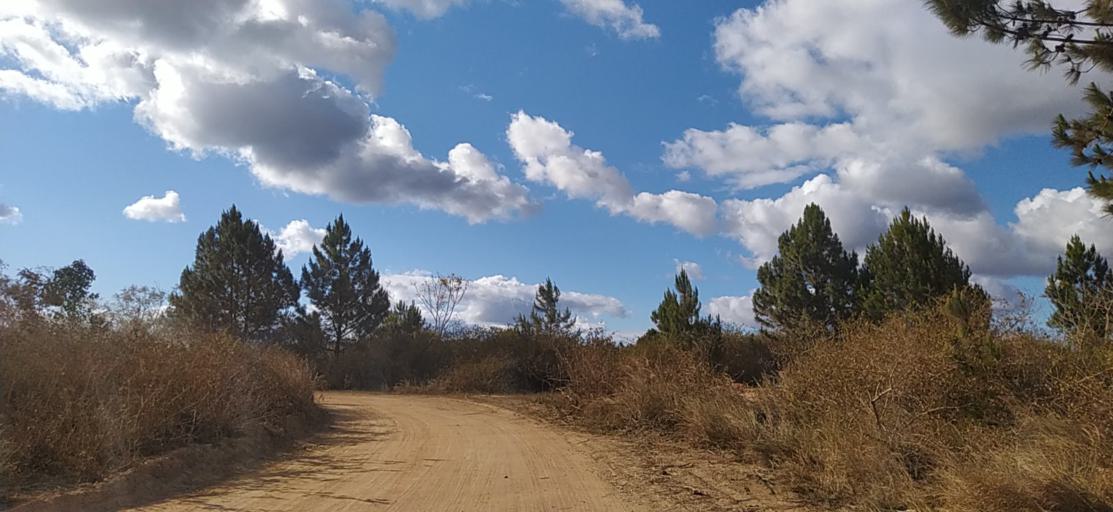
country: MG
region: Analamanga
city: Anjozorobe
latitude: -18.4999
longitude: 48.2676
